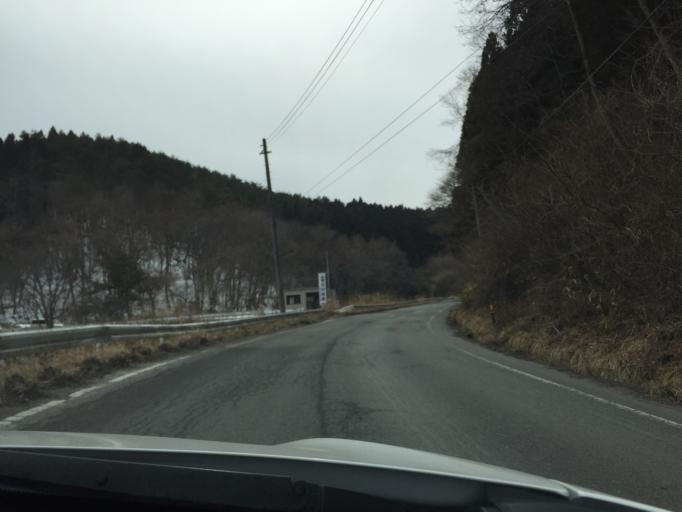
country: JP
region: Fukushima
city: Ishikawa
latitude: 37.1775
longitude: 140.6057
